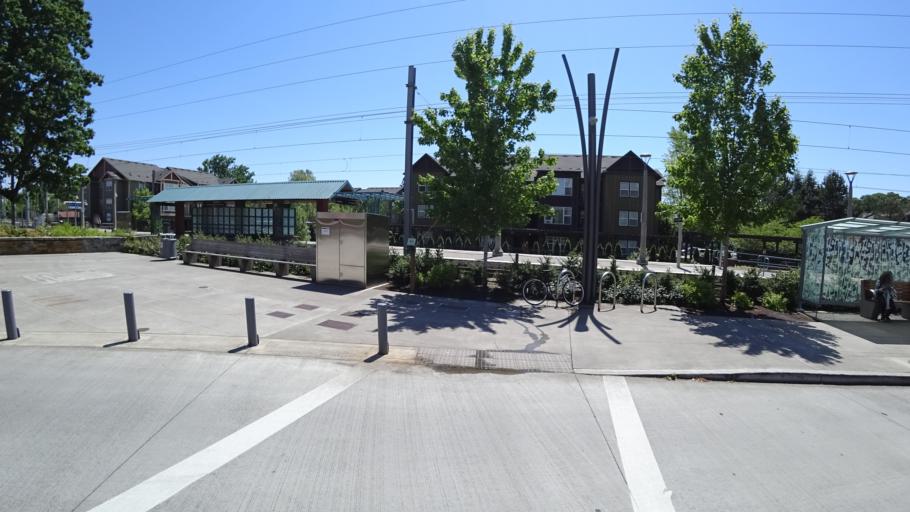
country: US
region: Oregon
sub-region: Washington County
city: Rockcreek
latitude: 45.5305
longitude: -122.9161
